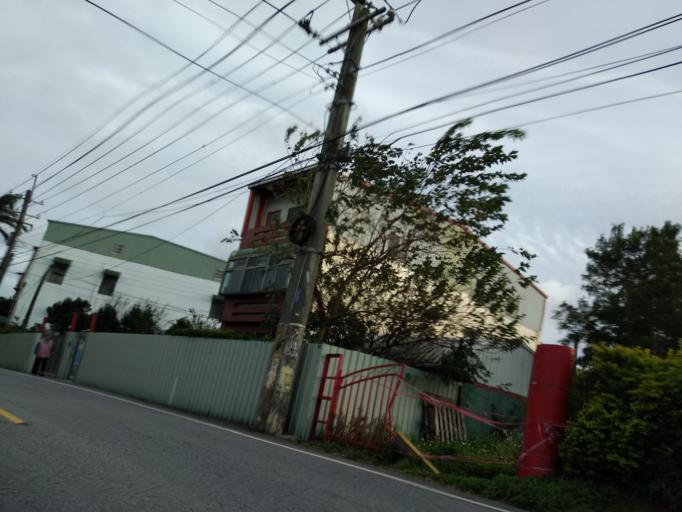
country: TW
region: Taiwan
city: Daxi
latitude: 24.9215
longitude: 121.1945
